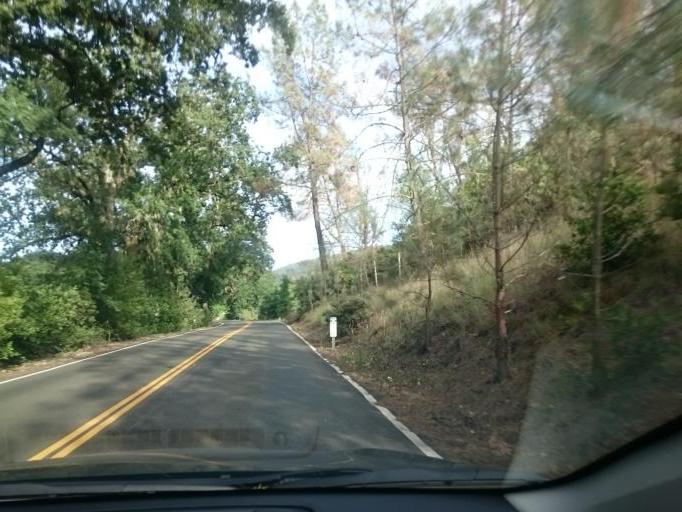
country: US
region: California
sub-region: Napa County
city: Yountville
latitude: 38.5044
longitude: -122.2924
